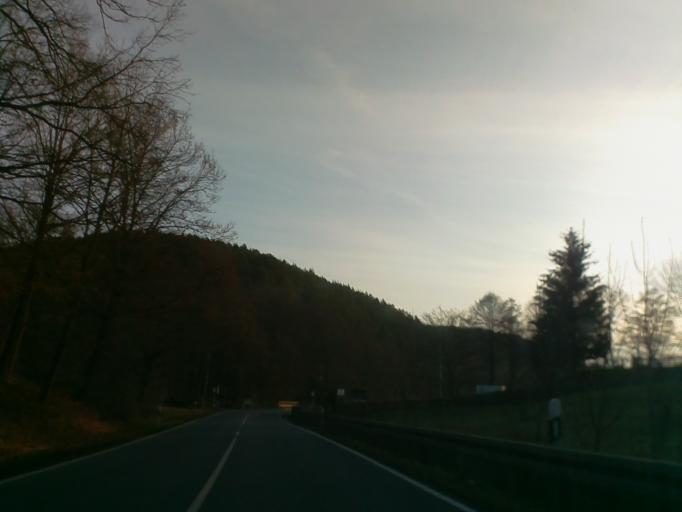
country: DE
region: Thuringia
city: Freienorla
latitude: 50.7508
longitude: 11.5566
